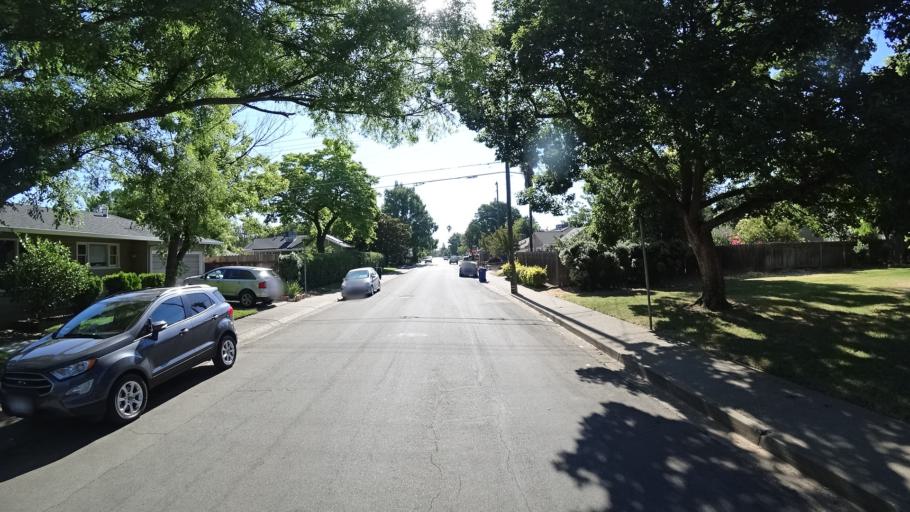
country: US
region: California
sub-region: Sacramento County
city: Florin
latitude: 38.5448
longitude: -121.4338
